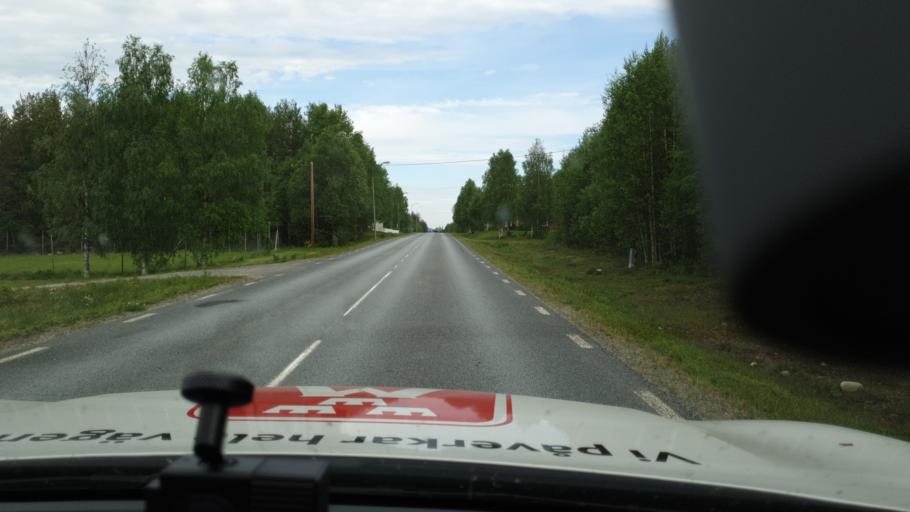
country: SE
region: Vaesterbotten
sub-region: Mala Kommun
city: Mala
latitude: 64.9935
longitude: 18.4884
